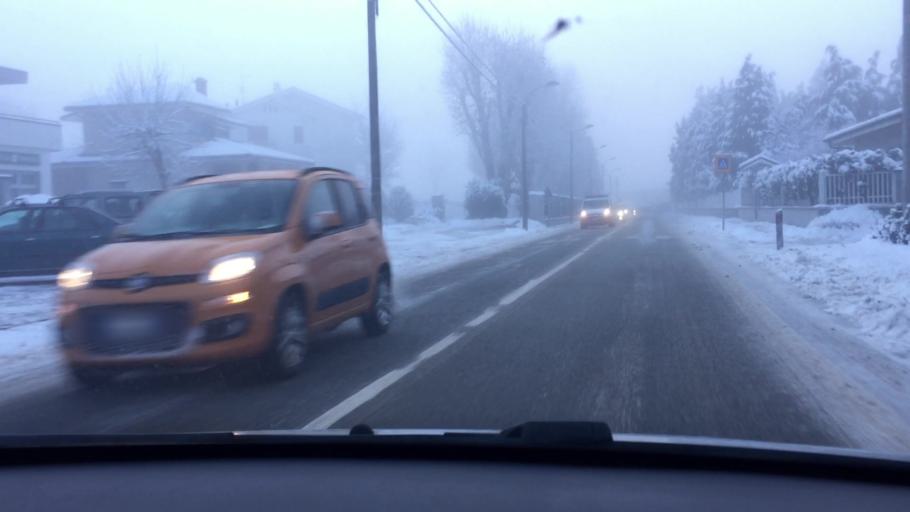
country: IT
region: Piedmont
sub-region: Provincia di Torino
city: Scalenghe
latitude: 44.8904
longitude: 7.4941
